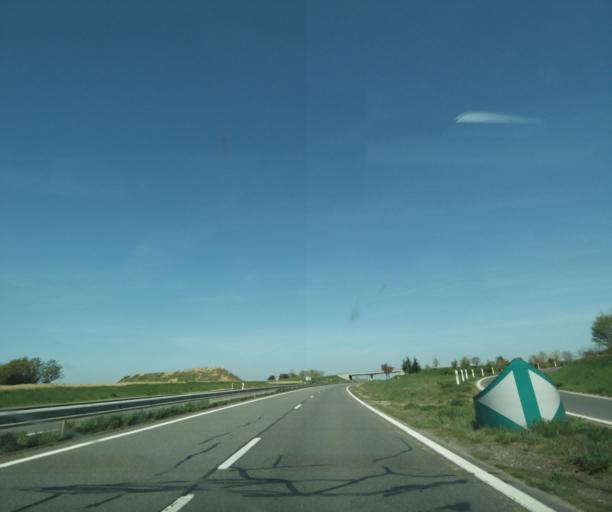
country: FR
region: Bourgogne
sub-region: Departement de la Nievre
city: Saint-Pierre-le-Moutier
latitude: 46.8003
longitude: 3.1199
